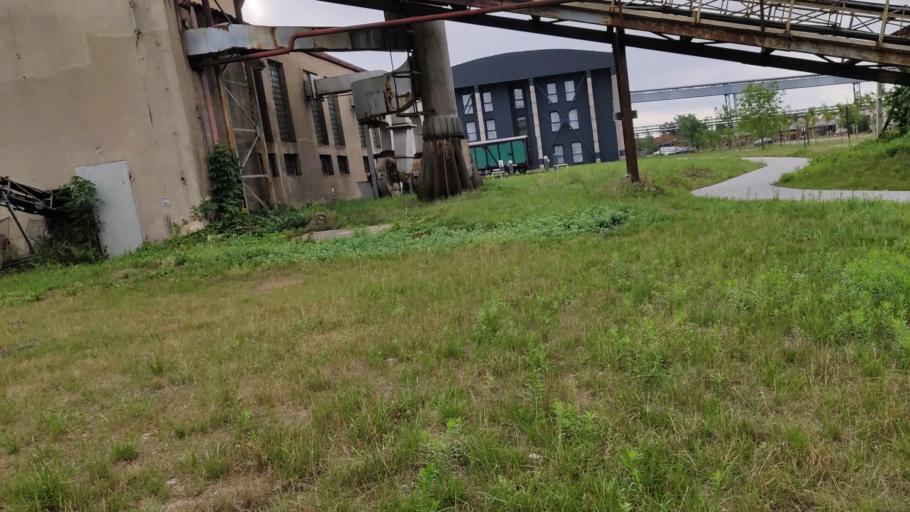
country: PL
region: Kujawsko-Pomorskie
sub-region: Powiat zninski
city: Znin
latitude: 52.8514
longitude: 17.7366
